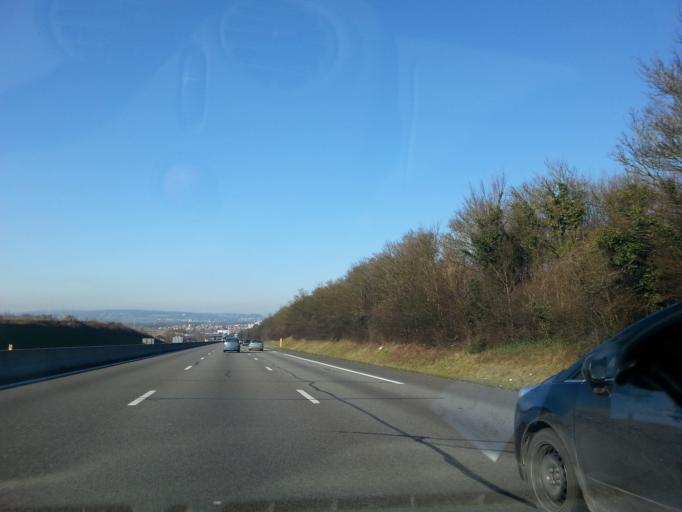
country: FR
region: Ile-de-France
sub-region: Departement des Yvelines
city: Chapet
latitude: 48.9595
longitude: 1.9323
